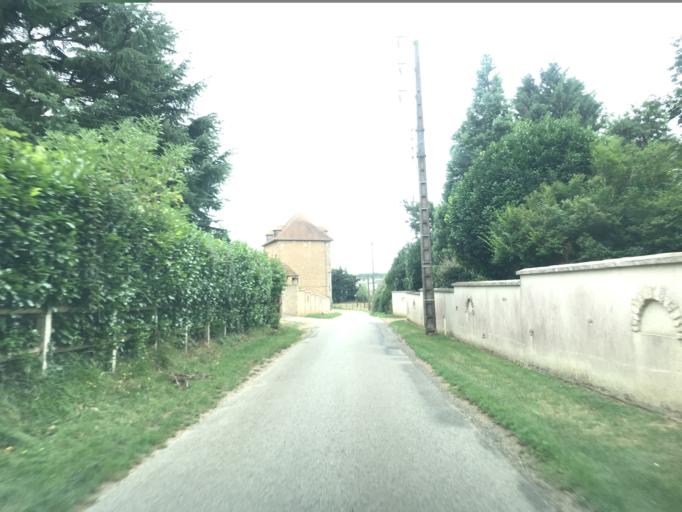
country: FR
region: Haute-Normandie
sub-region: Departement de l'Eure
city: Houlbec-Cocherel
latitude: 49.0547
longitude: 1.3525
